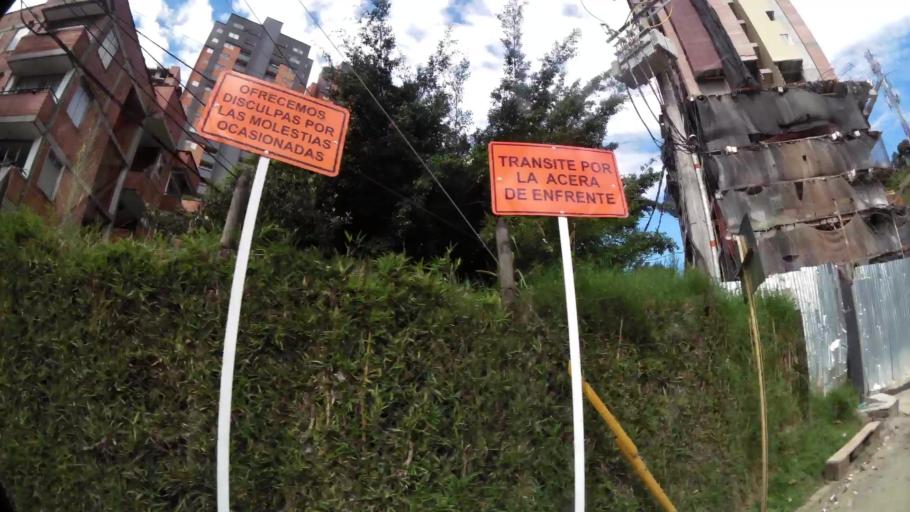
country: CO
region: Antioquia
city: Sabaneta
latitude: 6.1523
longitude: -75.6063
